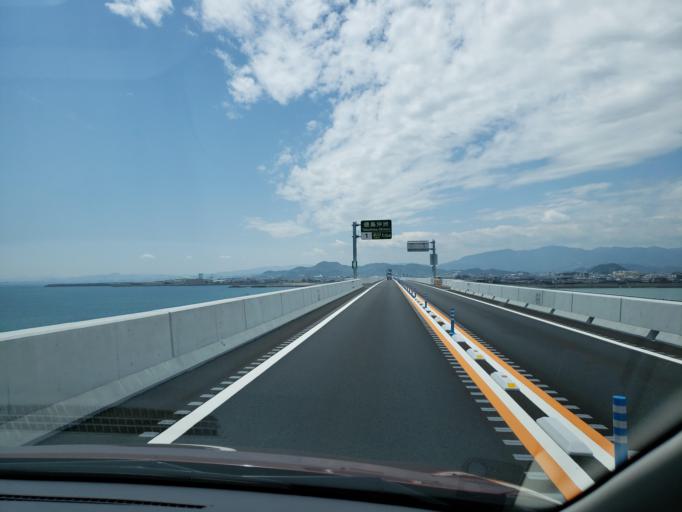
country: JP
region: Tokushima
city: Tokushima-shi
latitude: 34.0786
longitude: 134.6006
